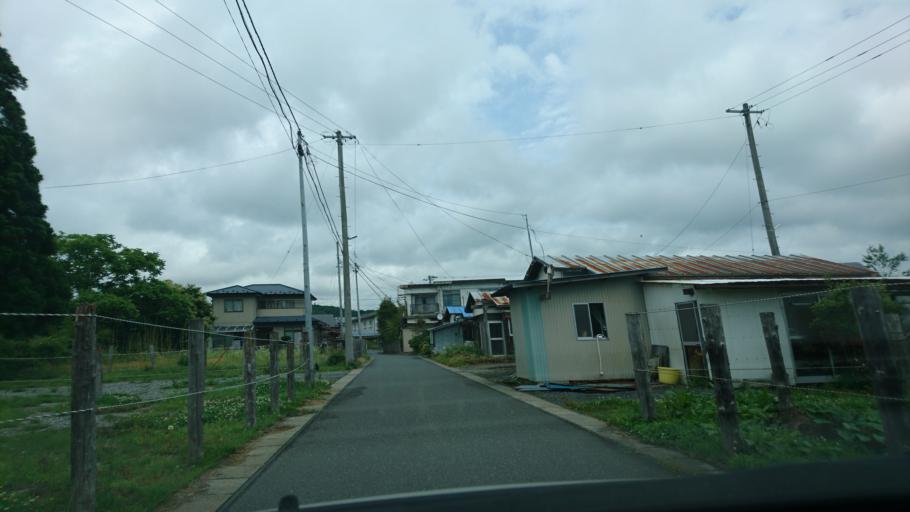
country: JP
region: Iwate
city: Ichinoseki
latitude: 38.9315
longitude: 141.1099
